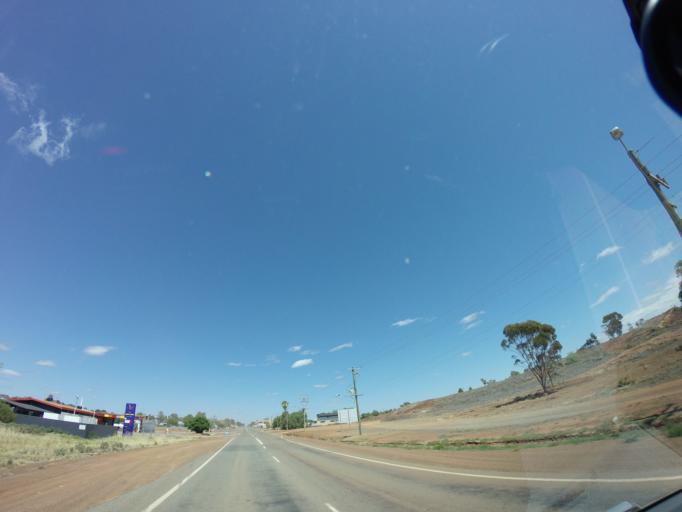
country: AU
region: Western Australia
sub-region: Kalgoorlie/Boulder
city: Boulder
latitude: -30.9547
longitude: 121.1735
